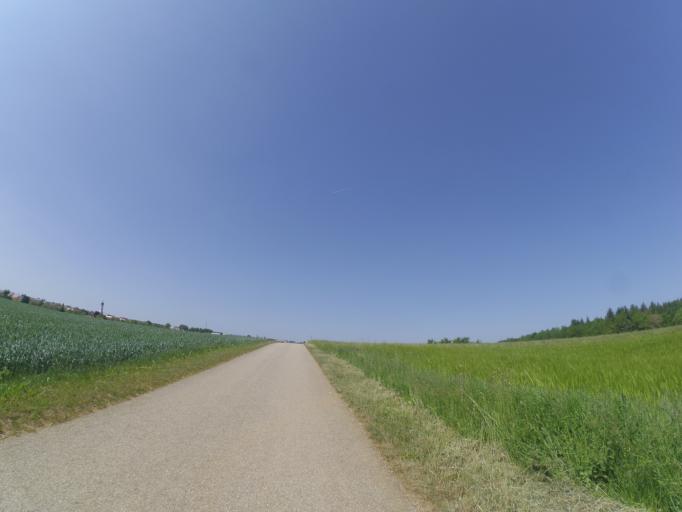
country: DE
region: Baden-Wuerttemberg
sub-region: Tuebingen Region
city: Merklingen
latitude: 48.5047
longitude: 9.7664
